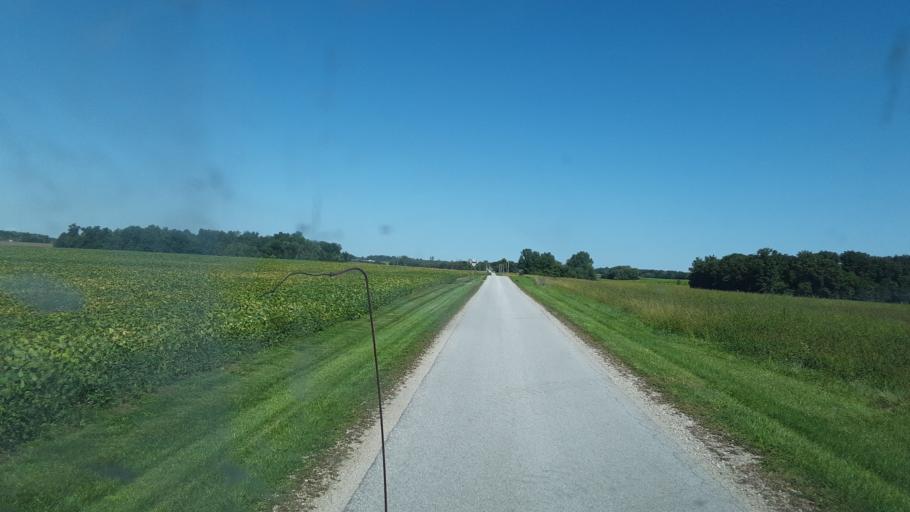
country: US
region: Ohio
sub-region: Sandusky County
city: Mount Carmel
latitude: 41.1912
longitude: -82.8991
